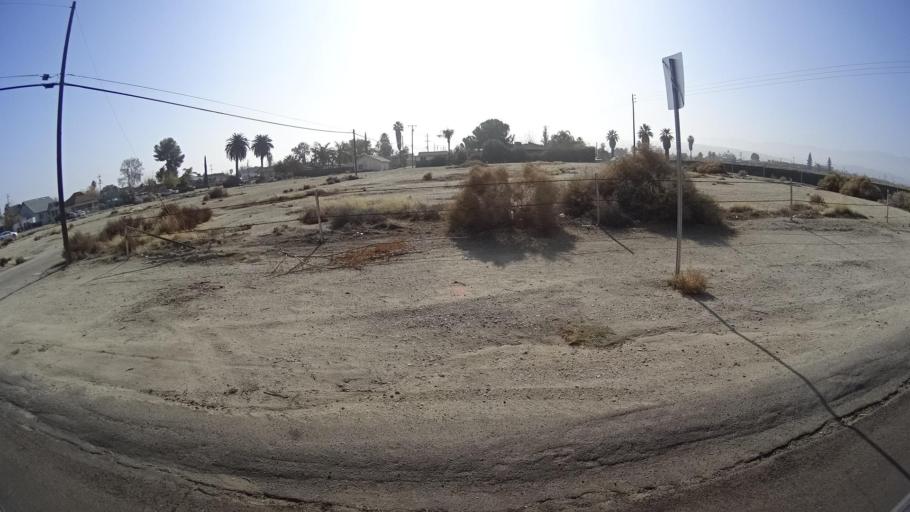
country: US
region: California
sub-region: Kern County
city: Ford City
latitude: 35.1545
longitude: -119.4648
